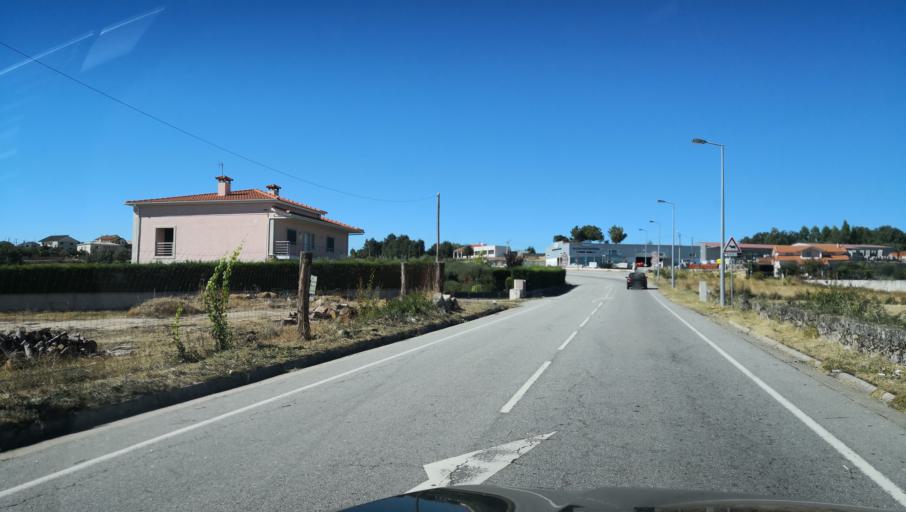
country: PT
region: Vila Real
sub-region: Valpacos
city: Valpacos
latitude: 41.6703
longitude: -7.3382
